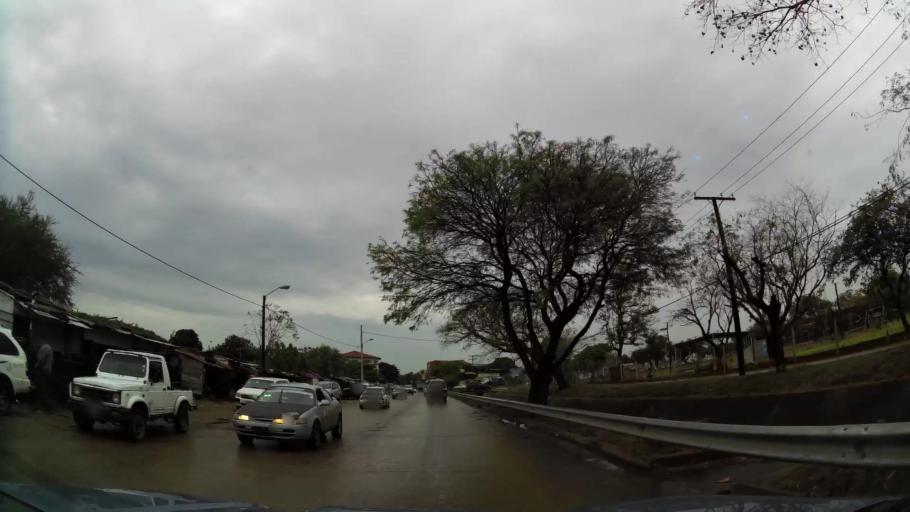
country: BO
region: Santa Cruz
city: Santa Cruz de la Sierra
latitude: -17.8097
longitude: -63.1960
